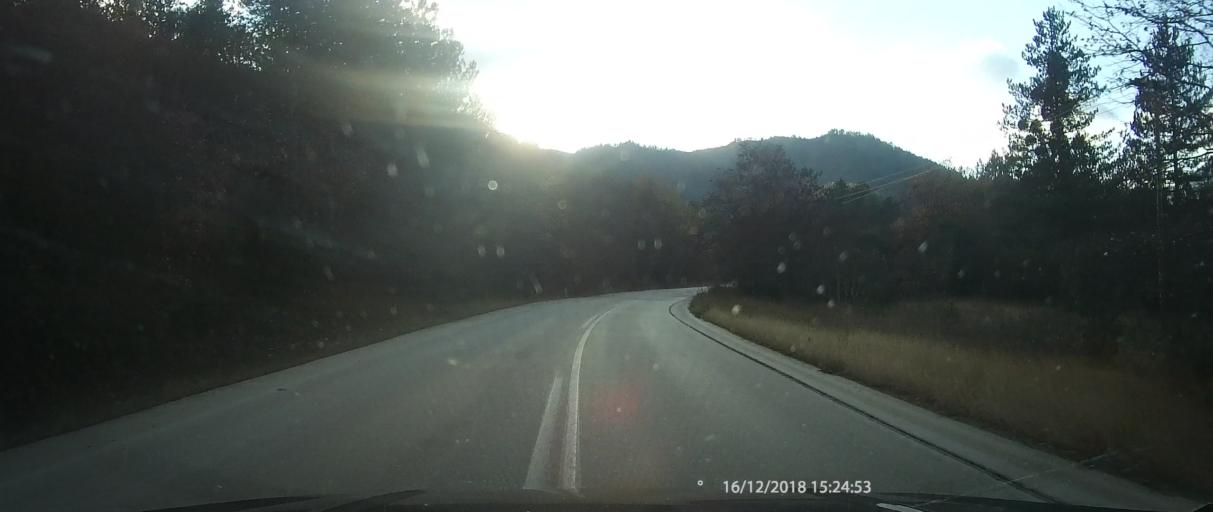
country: GR
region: Epirus
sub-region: Nomos Ioanninon
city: Konitsa
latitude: 40.1336
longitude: 20.7865
